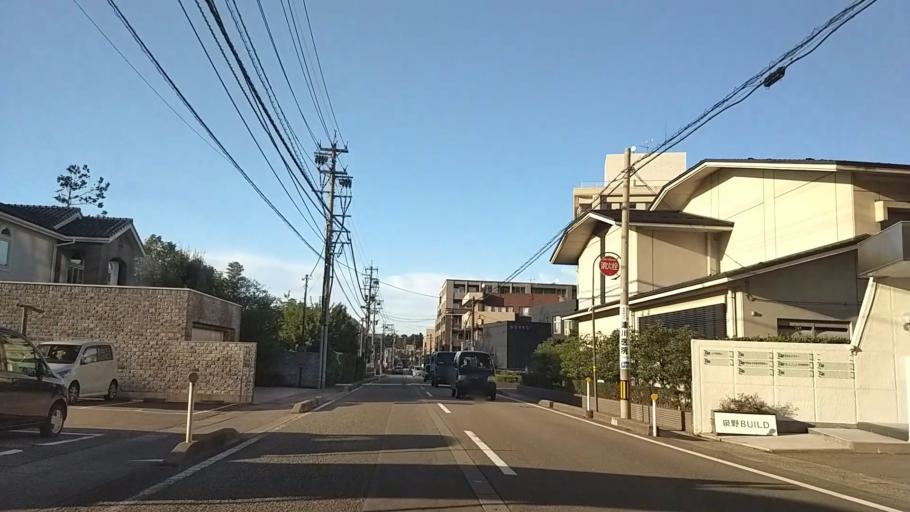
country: JP
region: Ishikawa
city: Nonoichi
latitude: 36.5459
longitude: 136.6490
